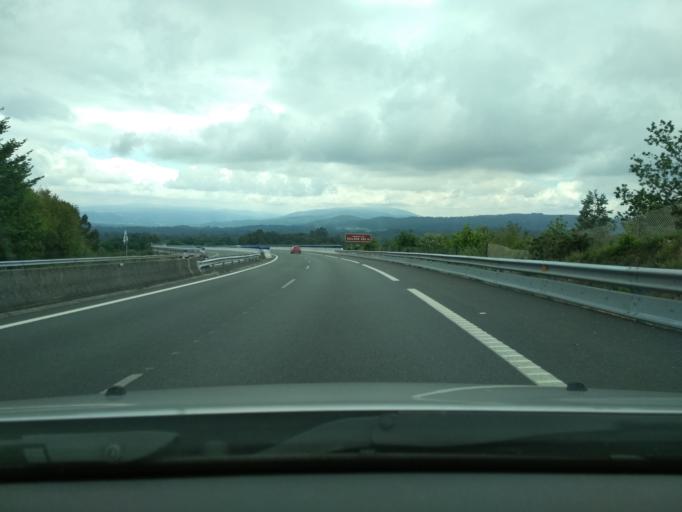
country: ES
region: Galicia
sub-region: Provincia da Coruna
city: Santiago de Compostela
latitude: 42.8351
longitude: -8.5731
